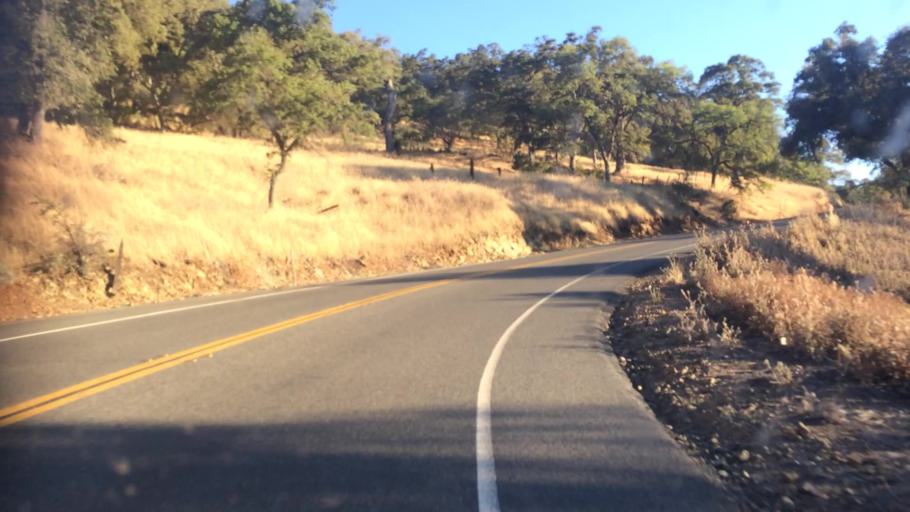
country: US
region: California
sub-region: El Dorado County
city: Deer Park
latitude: 38.6011
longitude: -120.8537
